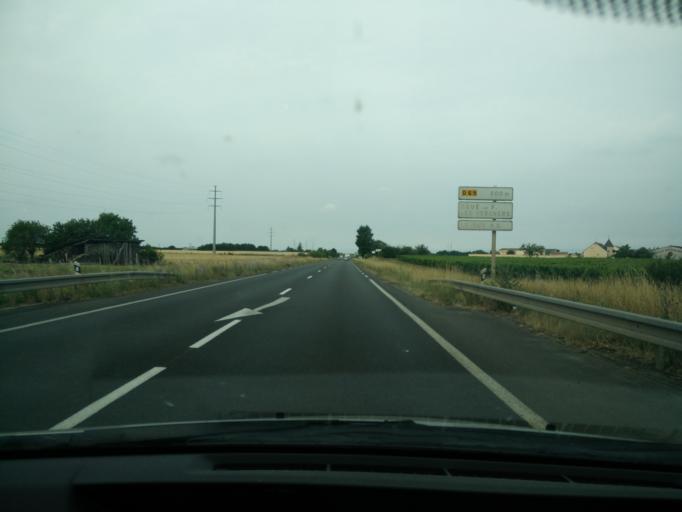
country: FR
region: Pays de la Loire
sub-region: Departement de Maine-et-Loire
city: Doue-la-Fontaine
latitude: 47.1820
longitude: -0.2541
